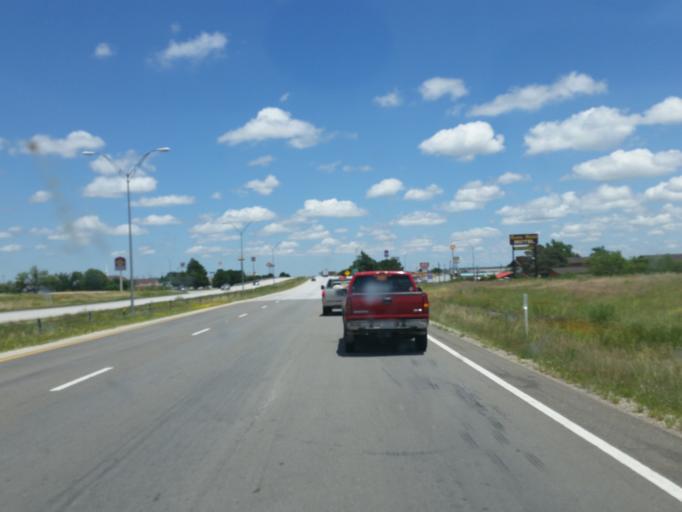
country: US
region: Texas
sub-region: Nolan County
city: Sweetwater
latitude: 32.4490
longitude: -100.4032
